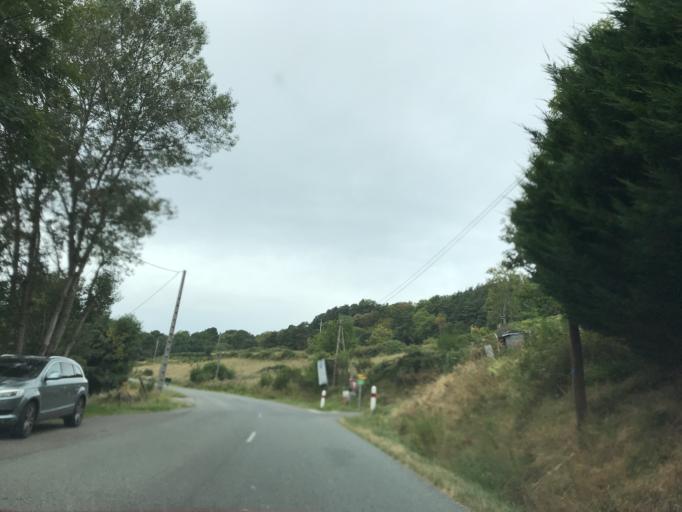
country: FR
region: Rhone-Alpes
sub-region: Departement de la Loire
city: Sail-sous-Couzan
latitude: 45.7004
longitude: 3.9257
